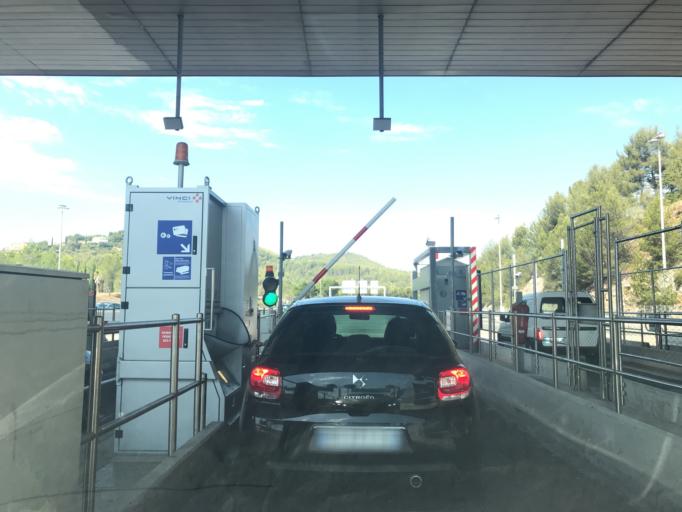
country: FR
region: Provence-Alpes-Cote d'Azur
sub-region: Departement du Var
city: Sanary-sur-Mer
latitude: 43.1467
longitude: 5.7719
